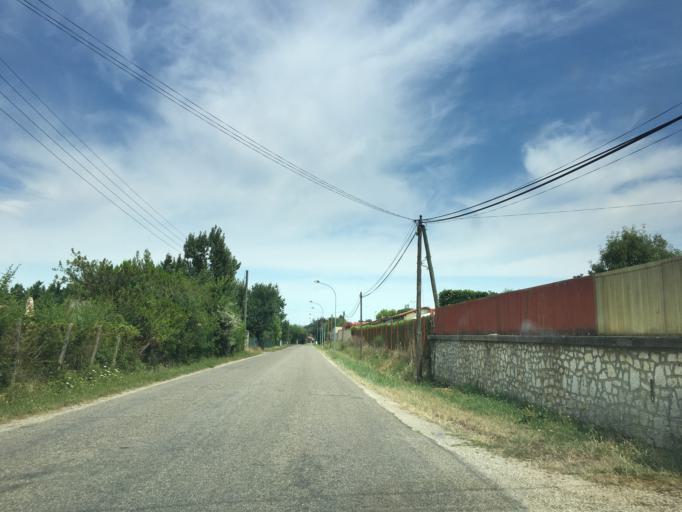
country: FR
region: Midi-Pyrenees
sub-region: Departement du Gers
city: Fleurance
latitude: 43.8396
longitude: 0.6513
